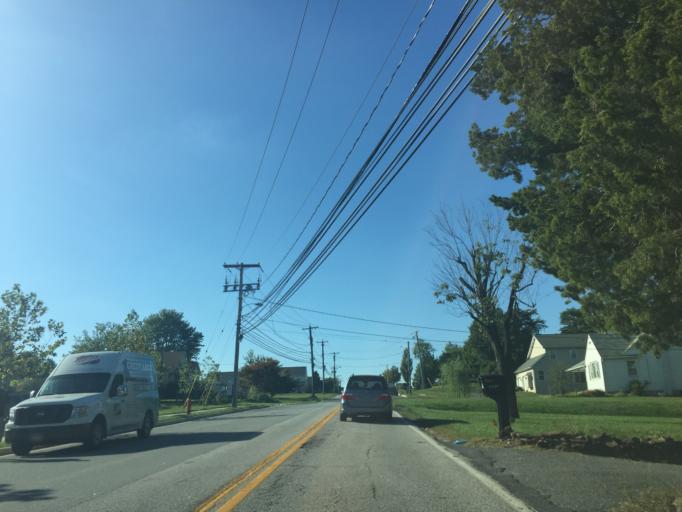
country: US
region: Maryland
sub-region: Baltimore County
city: Rossville
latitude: 39.3579
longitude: -76.4707
